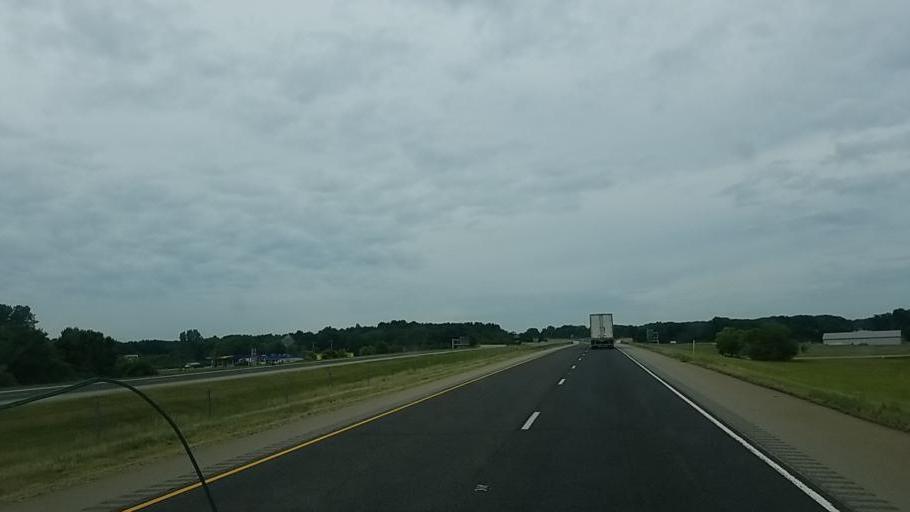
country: US
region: Indiana
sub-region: Steuben County
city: Angola
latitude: 41.6650
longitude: -85.0265
